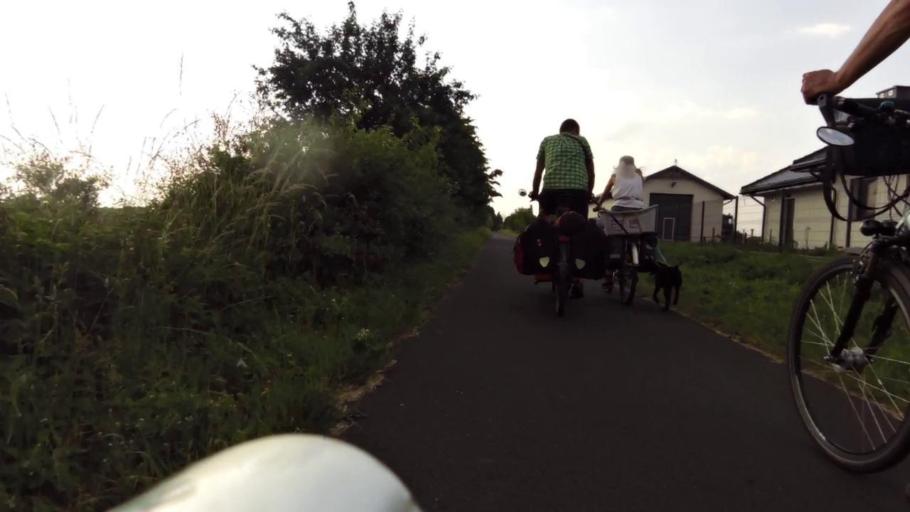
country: PL
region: Kujawsko-Pomorskie
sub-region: Powiat torunski
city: Lubianka
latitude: 53.1025
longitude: 18.5241
